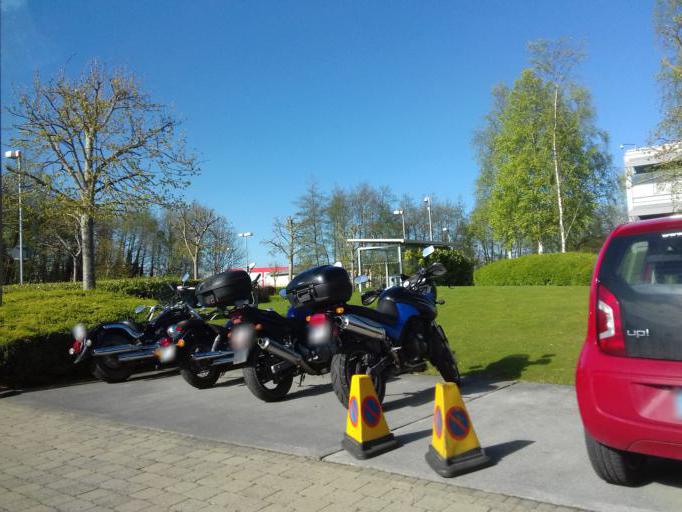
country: IE
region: Leinster
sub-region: Fingal County
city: Blanchardstown
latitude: 53.4087
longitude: -6.3605
